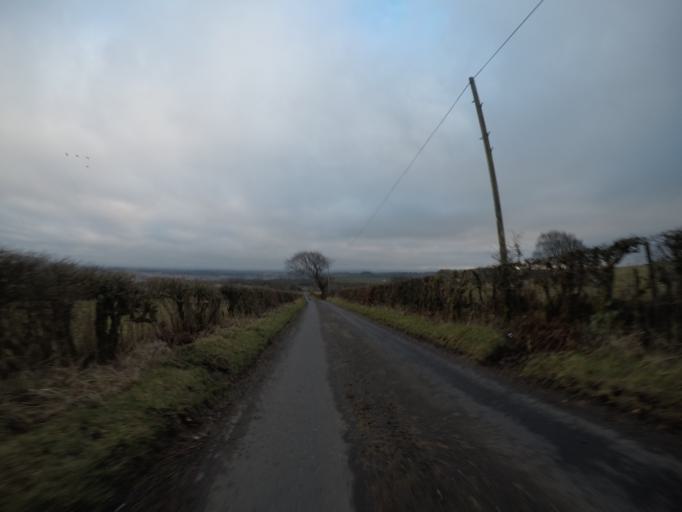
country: GB
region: Scotland
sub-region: North Ayrshire
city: Dalry
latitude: 55.7186
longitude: -4.7582
